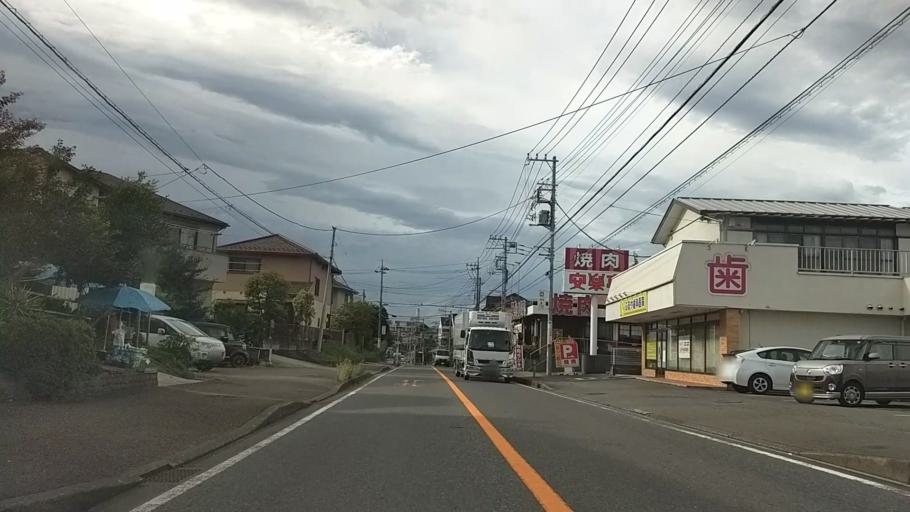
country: JP
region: Tokyo
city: Hachioji
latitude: 35.5691
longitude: 139.3419
